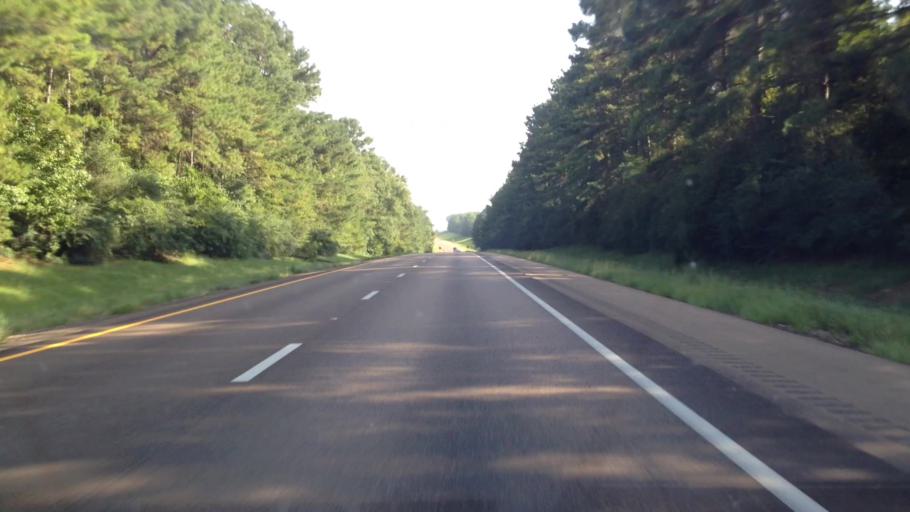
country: US
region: Mississippi
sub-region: Pike County
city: Summit
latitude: 31.4084
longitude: -90.4792
